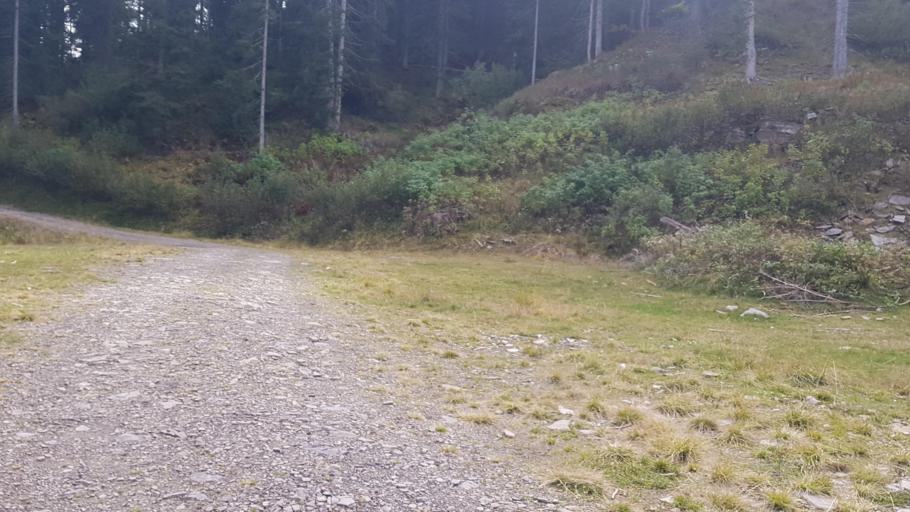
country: IT
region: Friuli Venezia Giulia
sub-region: Provincia di Udine
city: Pieria-Prato Carnico
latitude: 46.5051
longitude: 12.7495
